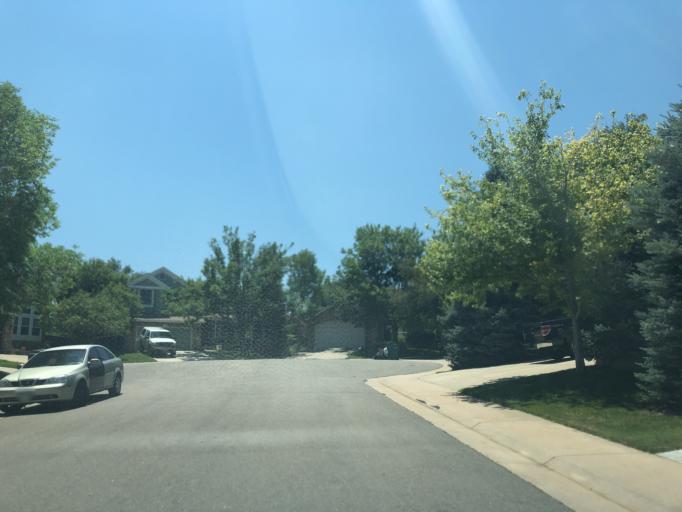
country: US
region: Colorado
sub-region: Arapahoe County
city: Dove Valley
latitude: 39.6232
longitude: -104.7588
